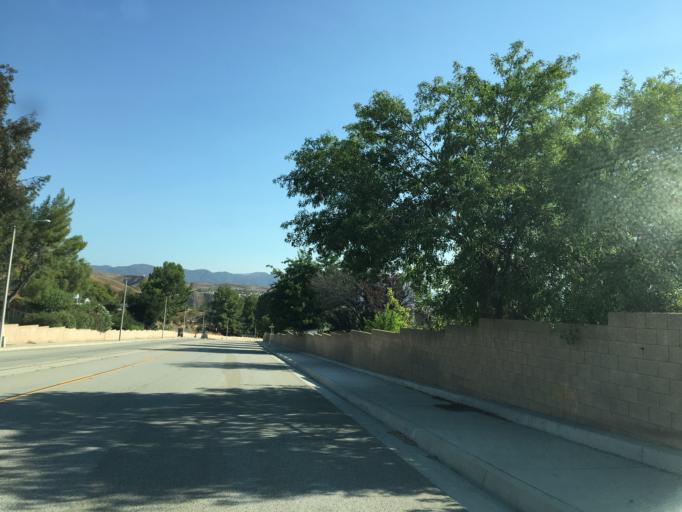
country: US
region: California
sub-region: Los Angeles County
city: Castaic
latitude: 34.4913
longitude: -118.6278
